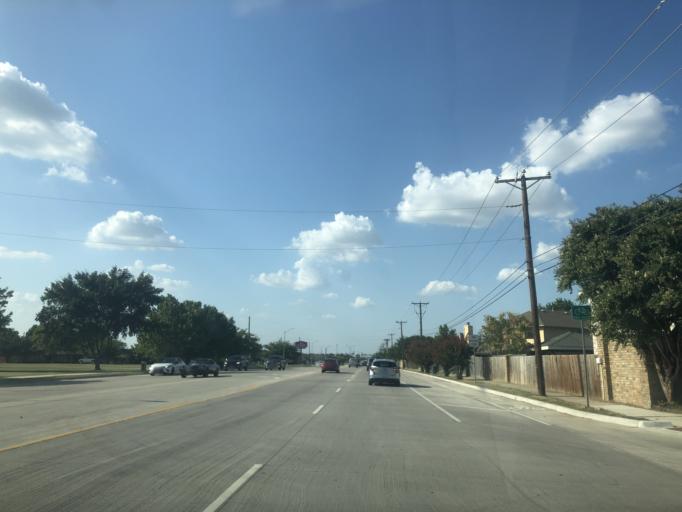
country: US
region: Texas
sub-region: Tarrant County
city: Saginaw
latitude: 32.8665
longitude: -97.3907
